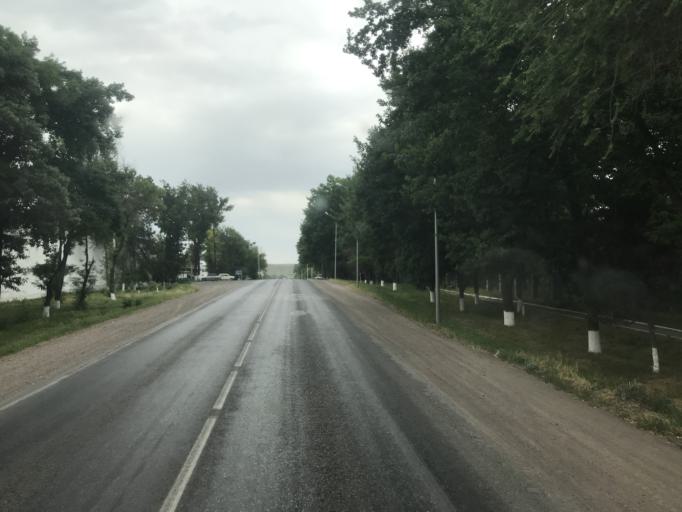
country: KZ
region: Ongtustik Qazaqstan
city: Saryaghash
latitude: 41.4907
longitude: 69.2748
